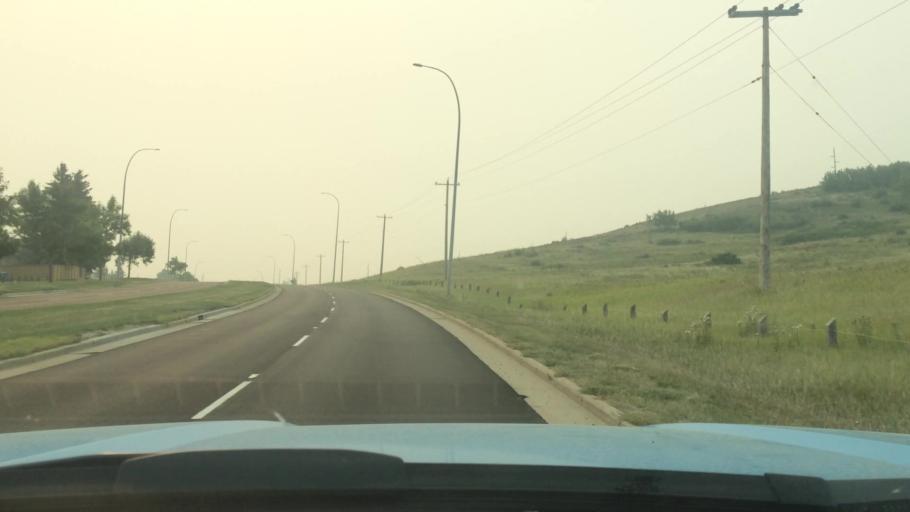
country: CA
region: Alberta
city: Calgary
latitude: 51.1281
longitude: -114.1042
